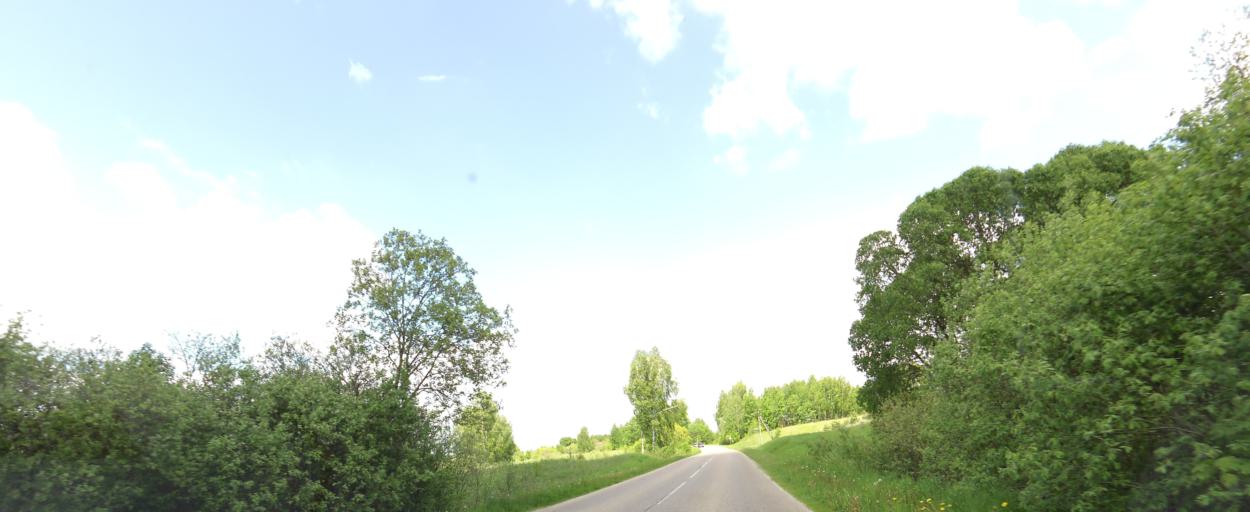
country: LT
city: Trakai
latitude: 54.6836
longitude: 24.9566
